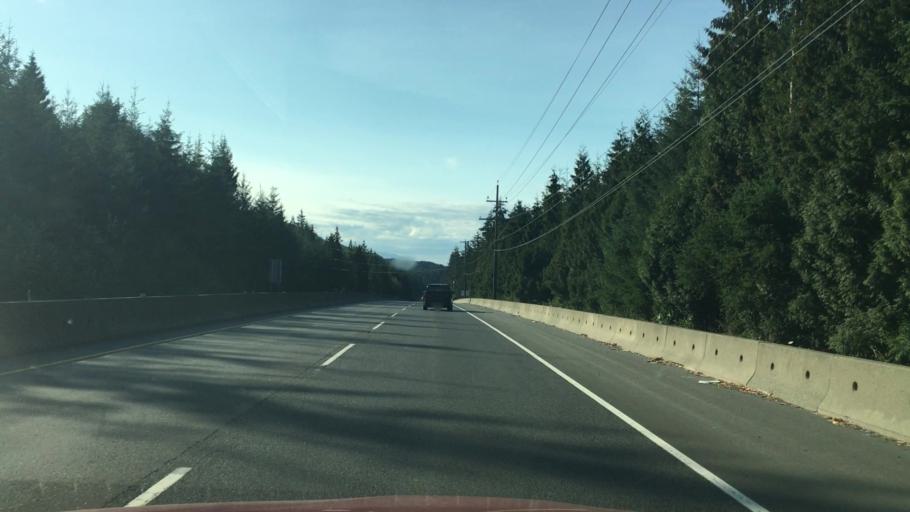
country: CA
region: British Columbia
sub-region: Cowichan Valley Regional District
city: Ladysmith
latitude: 48.9348
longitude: -123.7600
